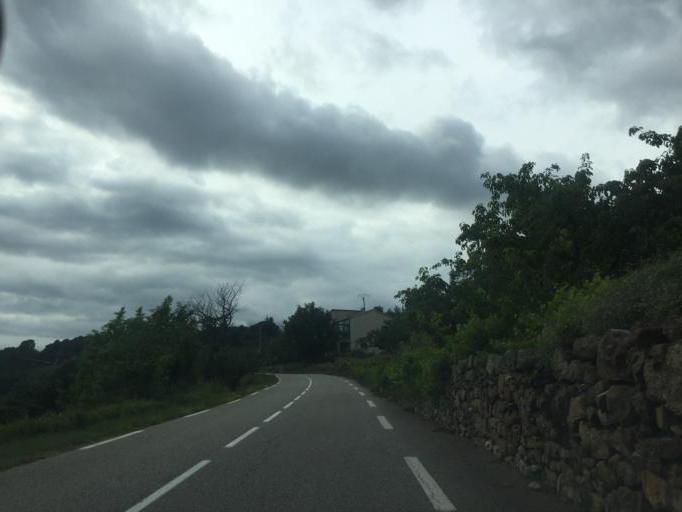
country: FR
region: Rhone-Alpes
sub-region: Departement de l'Ardeche
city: Privas
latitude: 44.7489
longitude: 4.5950
